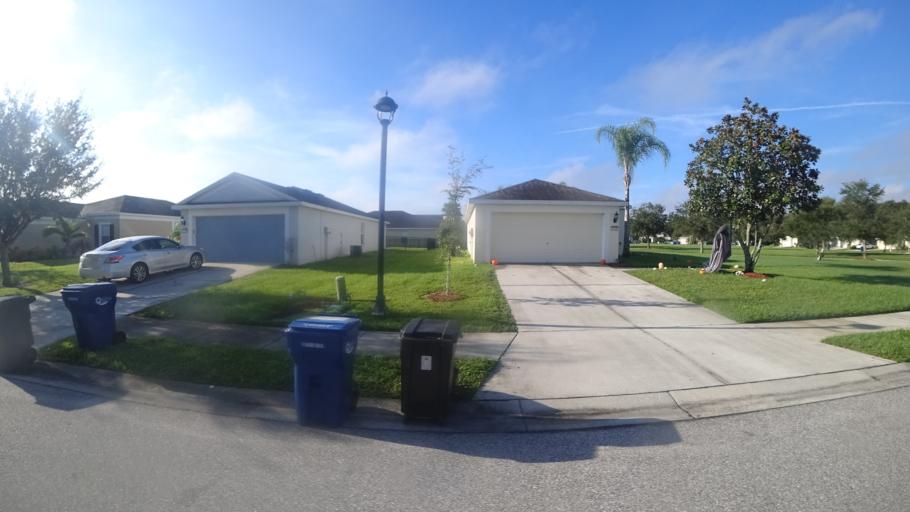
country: US
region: Florida
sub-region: Manatee County
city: Ellenton
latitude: 27.5607
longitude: -82.4652
